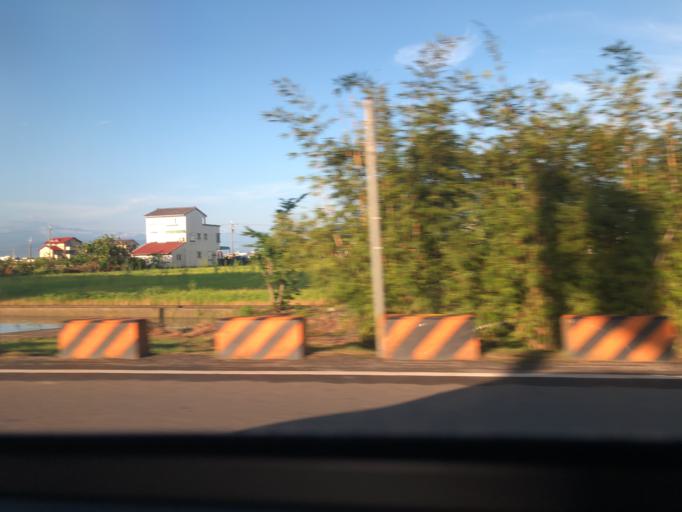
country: TW
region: Taiwan
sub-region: Yilan
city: Yilan
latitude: 24.7482
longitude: 121.7810
